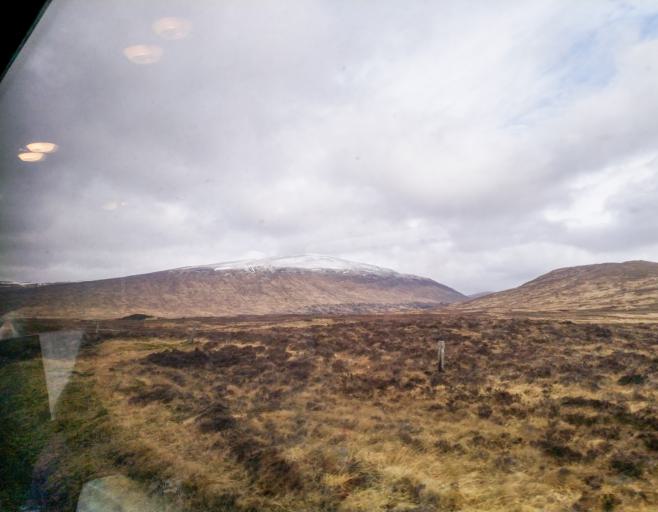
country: GB
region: Scotland
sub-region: Highland
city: Spean Bridge
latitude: 56.7472
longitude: -4.6727
